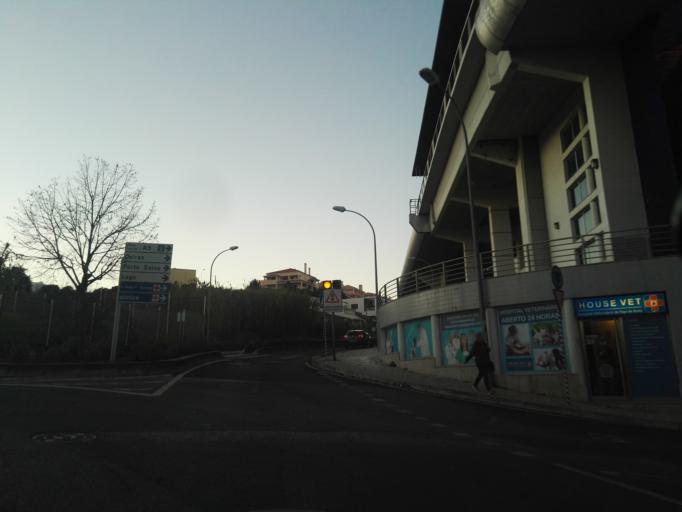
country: PT
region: Lisbon
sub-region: Oeiras
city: Paco de Arcos
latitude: 38.7006
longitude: -9.2955
